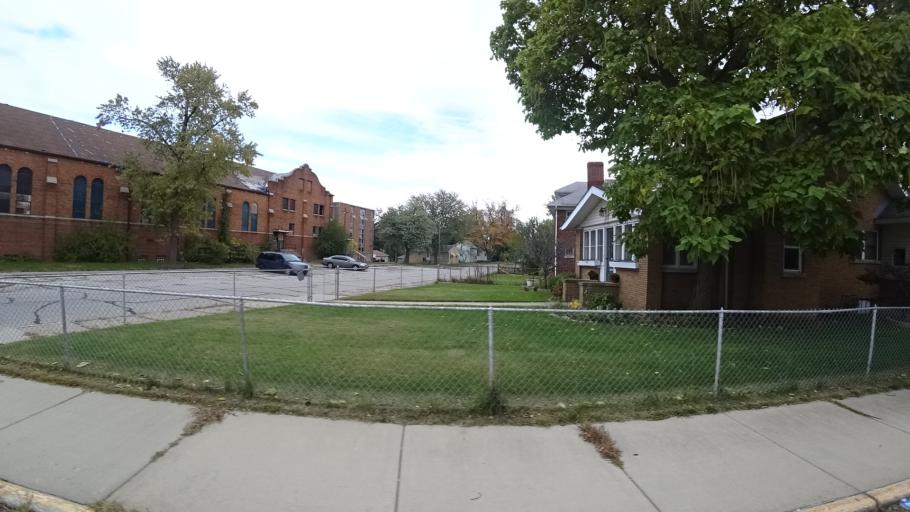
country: US
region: Indiana
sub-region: LaPorte County
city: Michigan City
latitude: 41.7120
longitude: -86.8946
